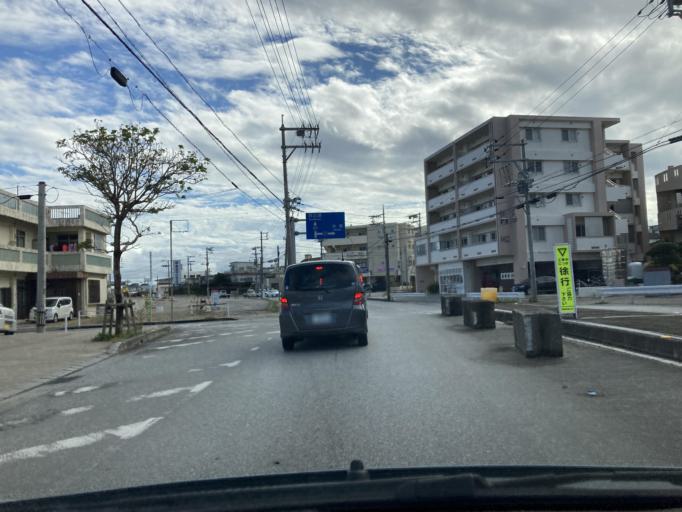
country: JP
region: Okinawa
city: Tomigusuku
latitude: 26.1540
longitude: 127.7210
